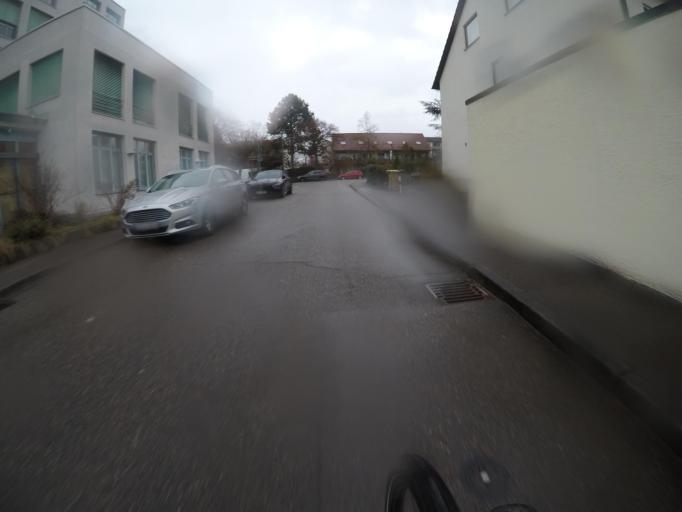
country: DE
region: Baden-Wuerttemberg
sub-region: Regierungsbezirk Stuttgart
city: Ludwigsburg
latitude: 48.9115
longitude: 9.1706
